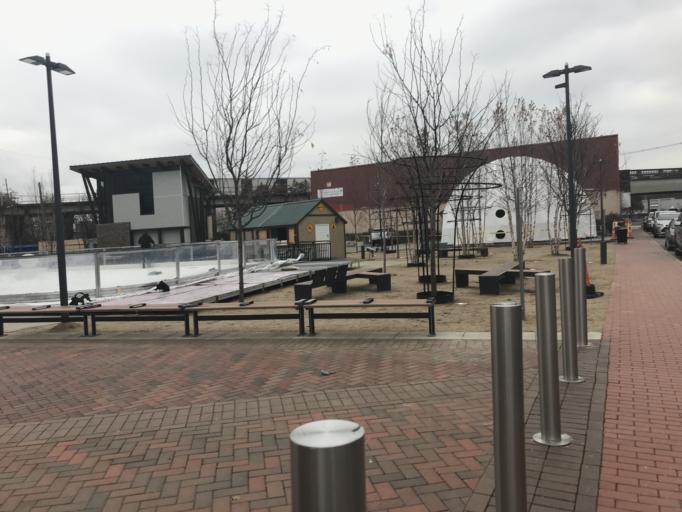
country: US
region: Kentucky
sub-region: Jefferson County
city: Louisville
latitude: 38.2430
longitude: -85.7349
